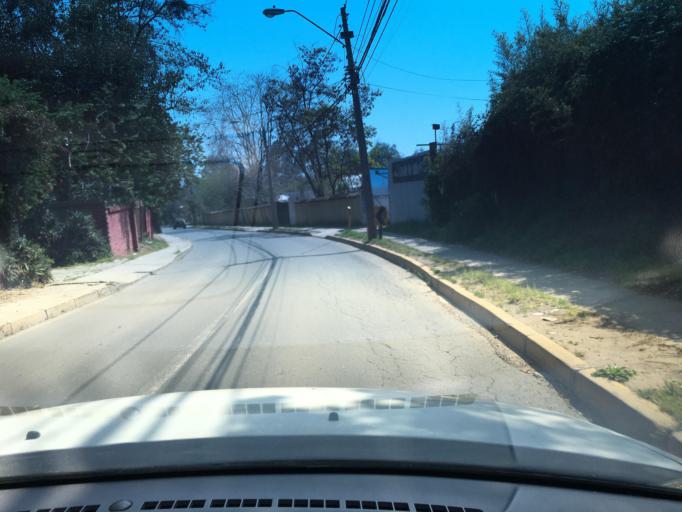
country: CL
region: Santiago Metropolitan
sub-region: Provincia de Santiago
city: Villa Presidente Frei, Nunoa, Santiago, Chile
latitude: -33.5145
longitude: -70.5443
